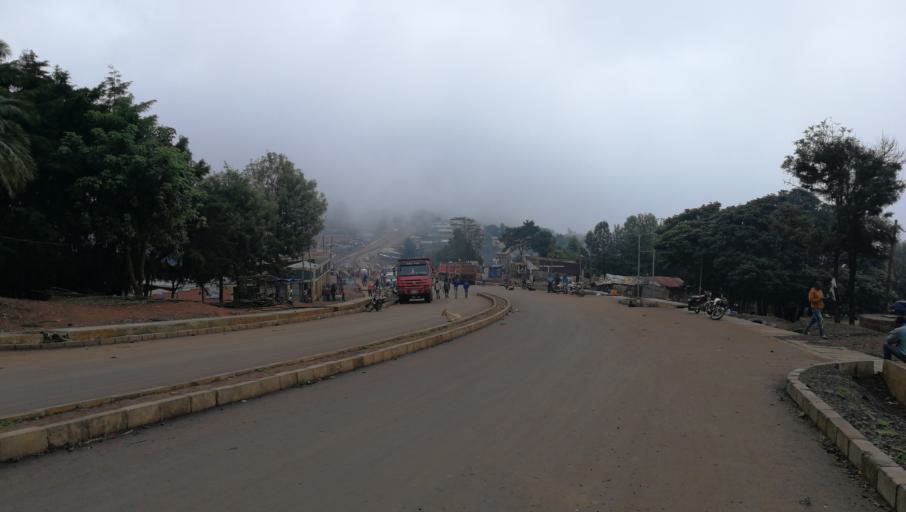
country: ET
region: Southern Nations, Nationalities, and People's Region
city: Areka
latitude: 7.0082
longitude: 37.2704
